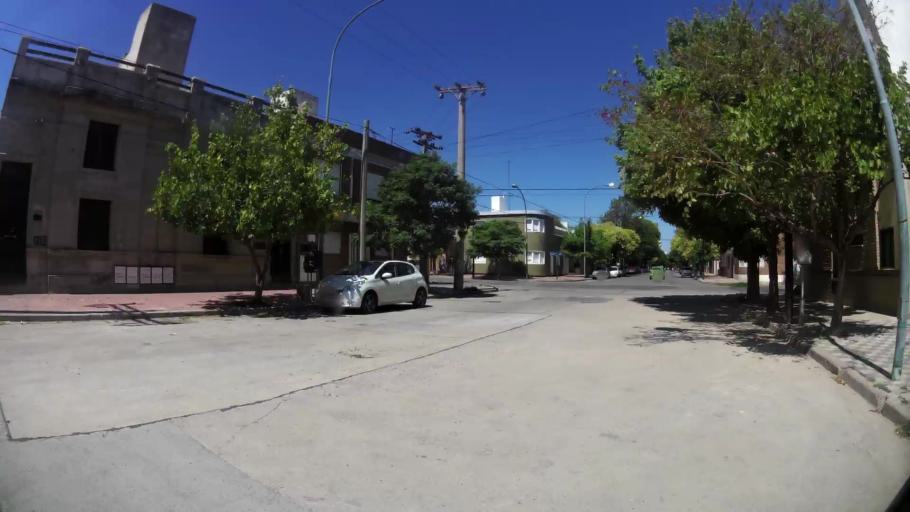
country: AR
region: Cordoba
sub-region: Departamento de Capital
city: Cordoba
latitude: -31.3948
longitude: -64.1931
